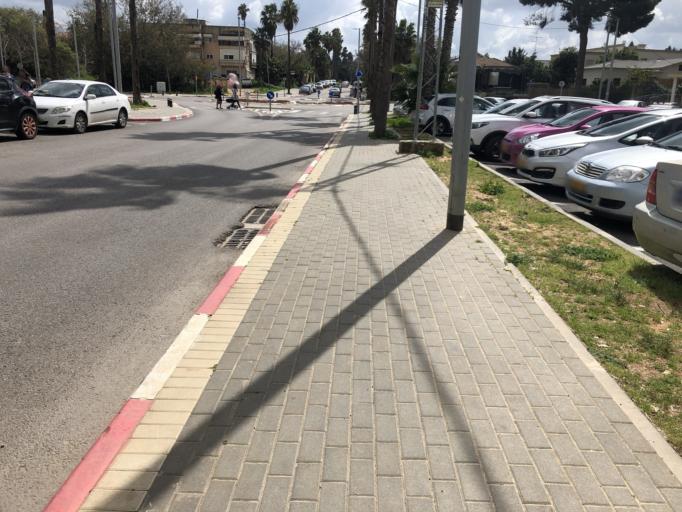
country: IL
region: Haifa
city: Hadera
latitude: 32.4731
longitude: 34.9739
